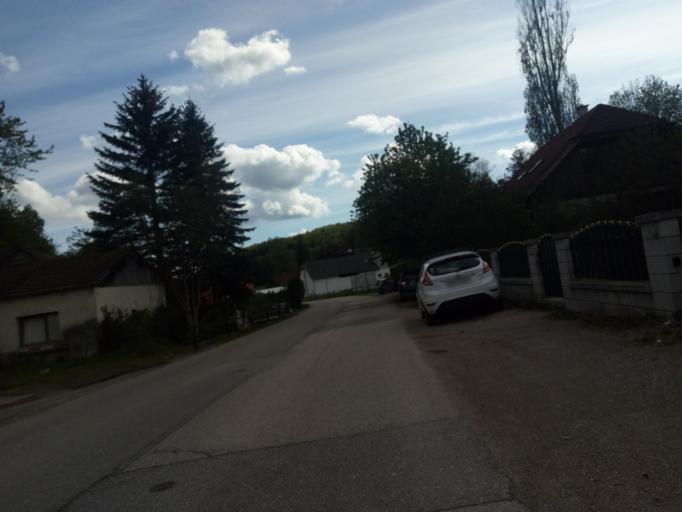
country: AT
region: Lower Austria
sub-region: Politischer Bezirk Wien-Umgebung
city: Wolfsgraben
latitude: 48.1282
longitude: 16.0966
